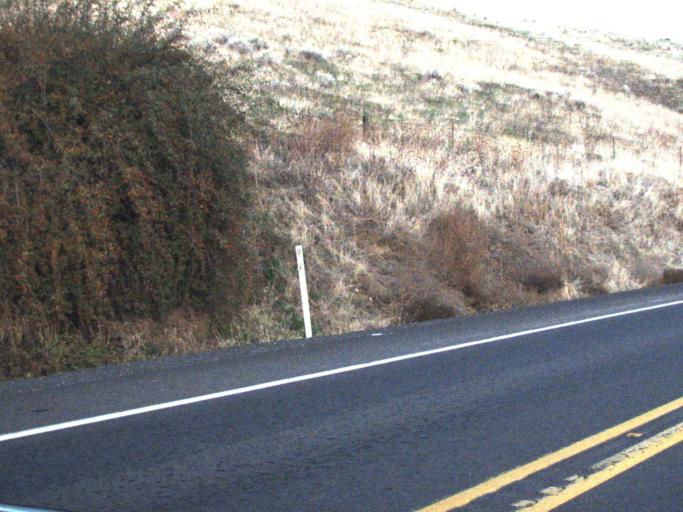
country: US
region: Washington
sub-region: Garfield County
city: Pomeroy
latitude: 46.6558
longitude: -117.8061
